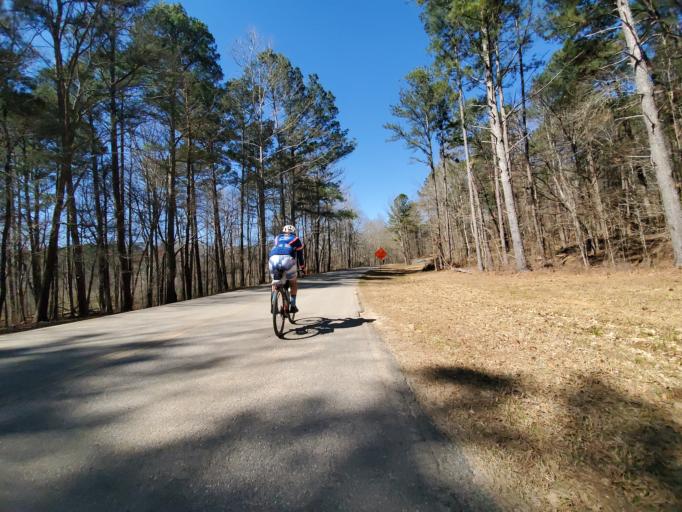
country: US
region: Georgia
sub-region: Barrow County
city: Winder
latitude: 33.9819
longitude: -83.7294
